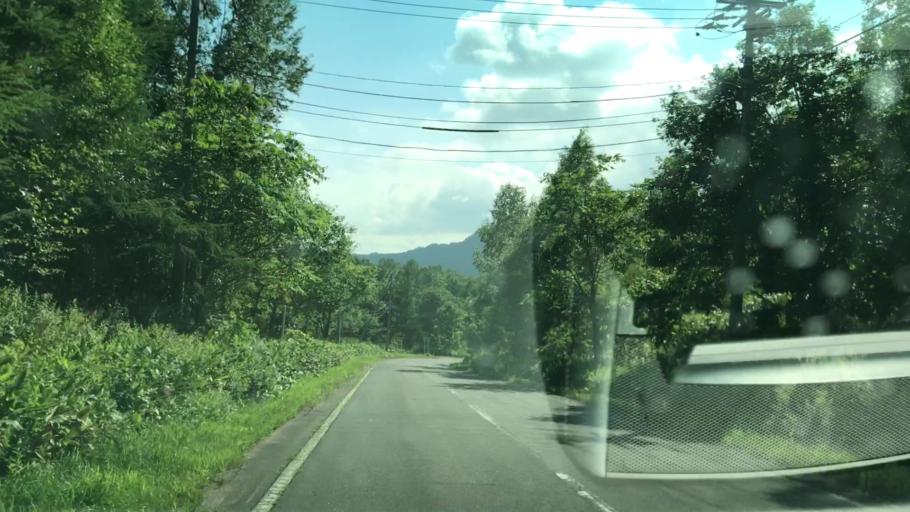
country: JP
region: Hokkaido
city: Shimo-furano
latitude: 42.8521
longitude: 142.4351
